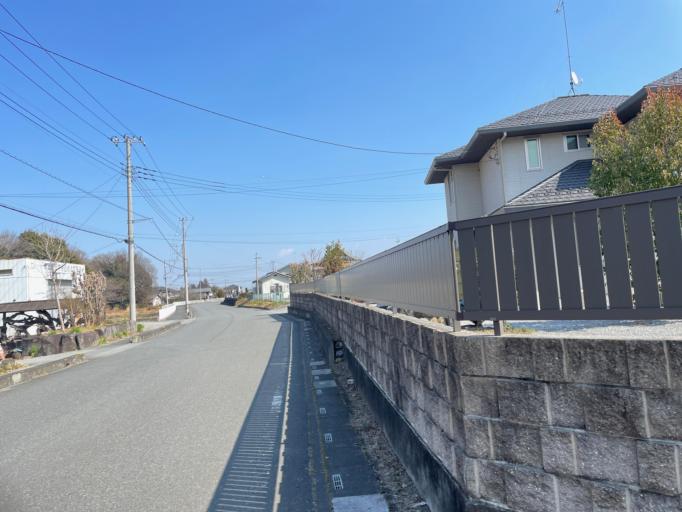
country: JP
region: Saitama
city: Yorii
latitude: 36.1143
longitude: 139.2237
